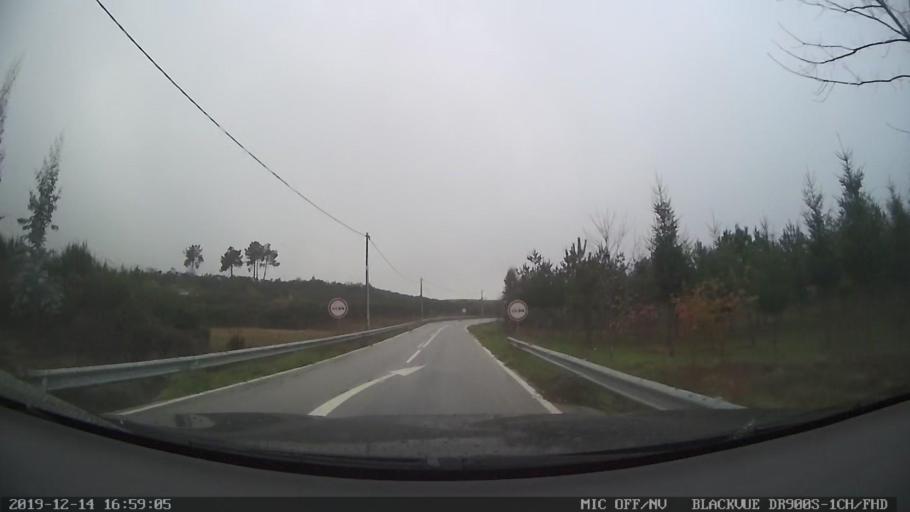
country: PT
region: Vila Real
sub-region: Vila Pouca de Aguiar
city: Vila Pouca de Aguiar
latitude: 41.4351
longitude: -7.5588
